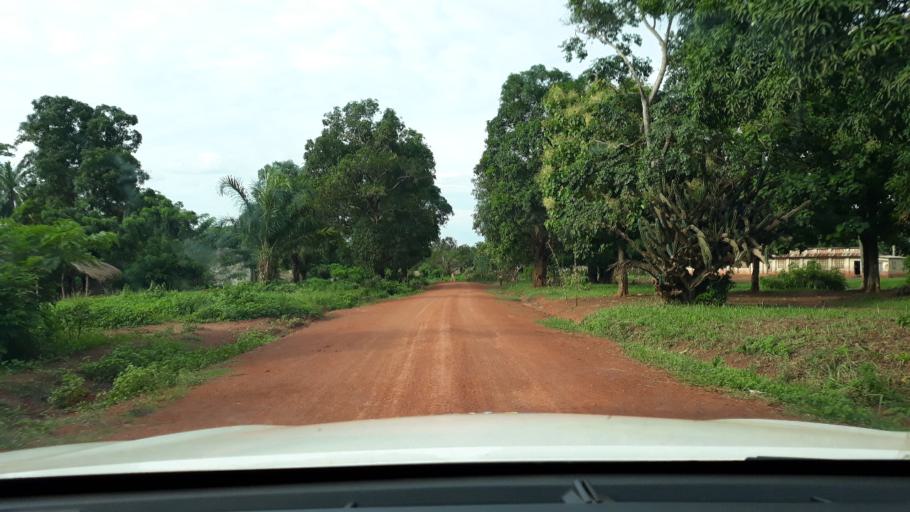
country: CD
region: Equateur
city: Libenge
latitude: 3.8924
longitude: 18.6897
